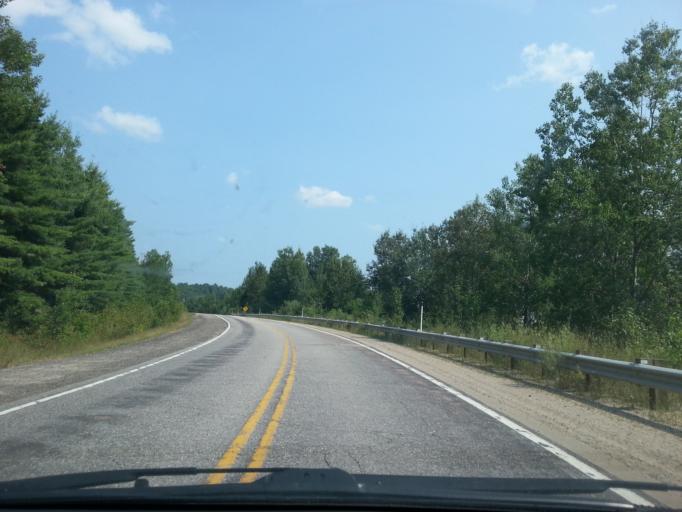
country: CA
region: Quebec
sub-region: Outaouais
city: Maniwaki
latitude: 46.1053
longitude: -76.1158
